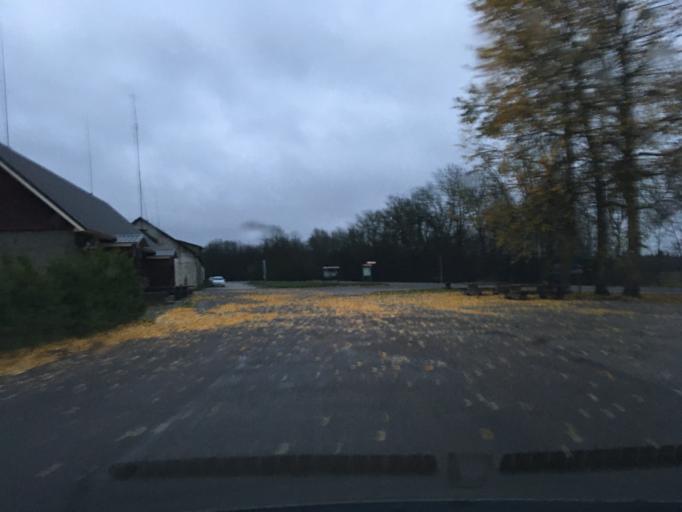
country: EE
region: Laeaene
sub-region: Lihula vald
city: Lihula
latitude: 58.5729
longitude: 23.7418
